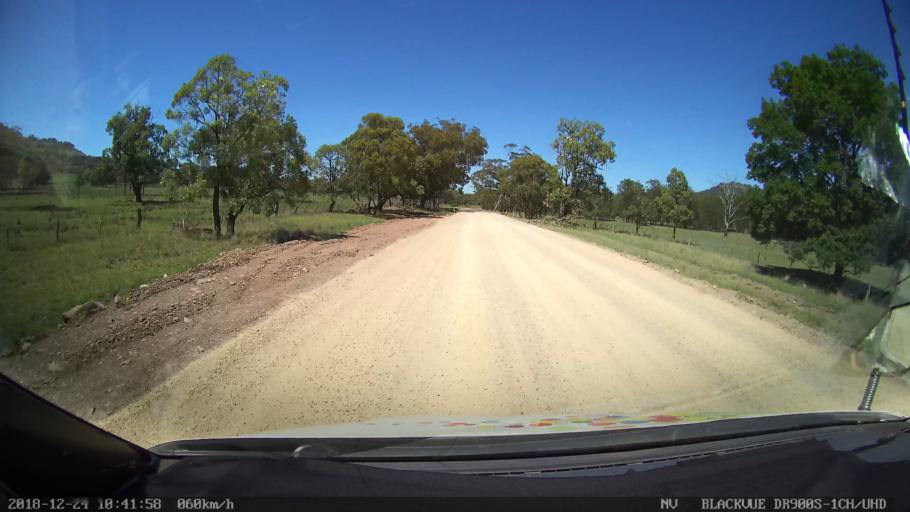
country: AU
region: New South Wales
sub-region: Upper Hunter Shire
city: Merriwa
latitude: -31.8730
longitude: 150.4559
